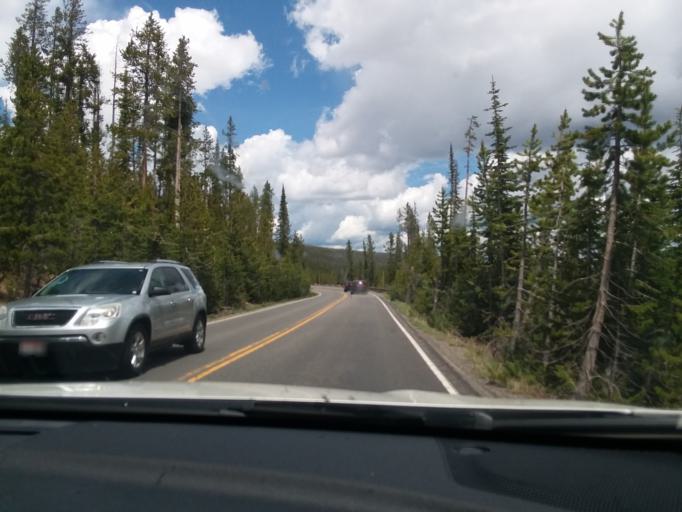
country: US
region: Montana
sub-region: Gallatin County
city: West Yellowstone
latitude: 44.2026
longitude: -110.6600
